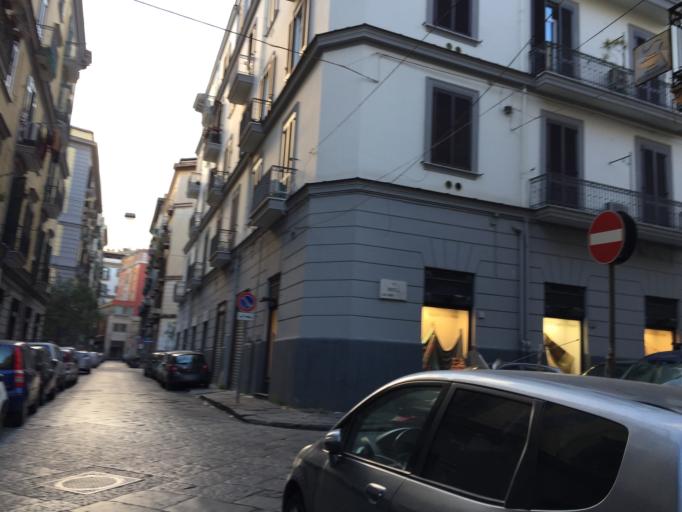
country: IT
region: Campania
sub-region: Provincia di Napoli
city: Napoli
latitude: 40.8468
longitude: 14.2627
